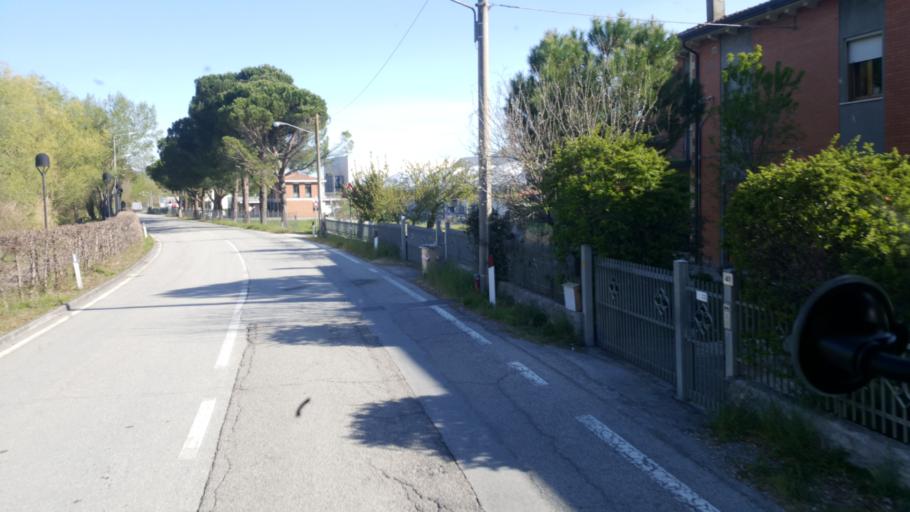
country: SM
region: Acquaviva
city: Acquaviva
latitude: 43.9477
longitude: 12.4056
